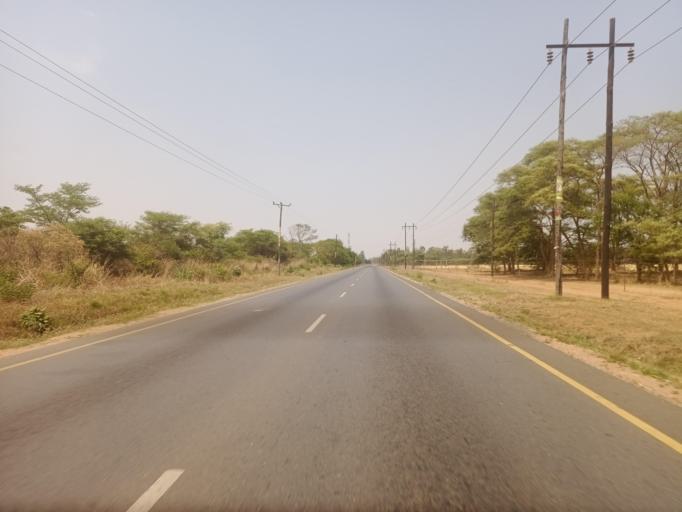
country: ZM
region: Lusaka
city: Lusaka
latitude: -15.2832
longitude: 28.3870
